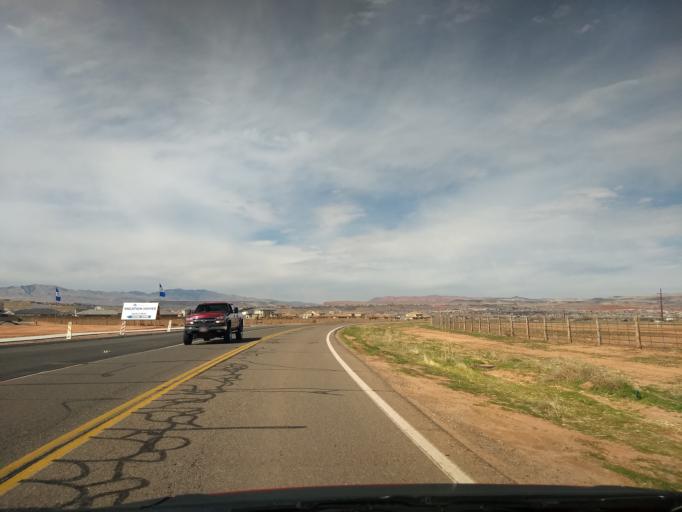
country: US
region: Utah
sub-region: Washington County
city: Washington
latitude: 37.0780
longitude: -113.4971
